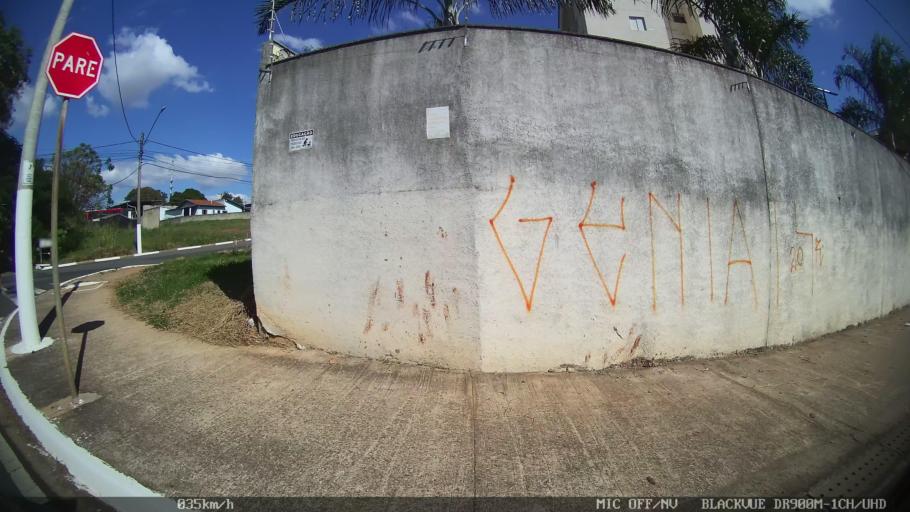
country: BR
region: Sao Paulo
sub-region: Hortolandia
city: Hortolandia
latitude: -22.8970
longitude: -47.1939
